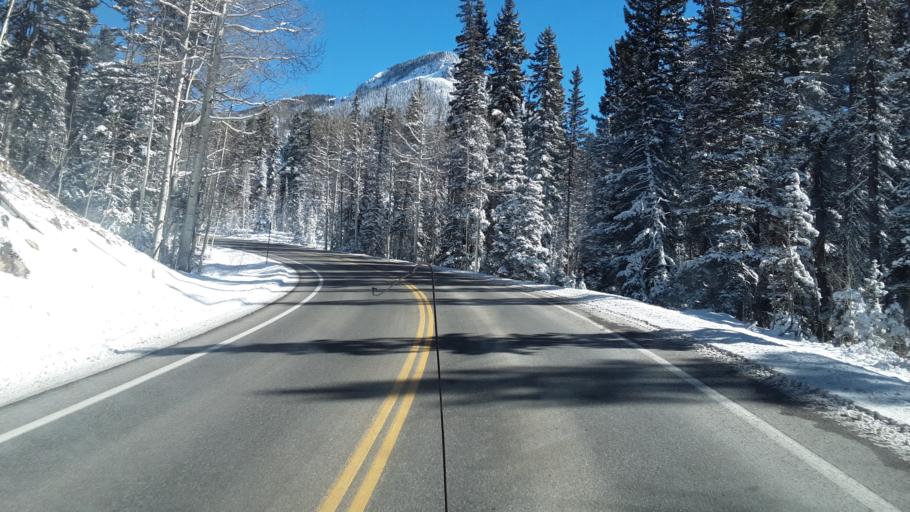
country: US
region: Colorado
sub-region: San Juan County
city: Silverton
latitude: 37.6730
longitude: -107.7919
